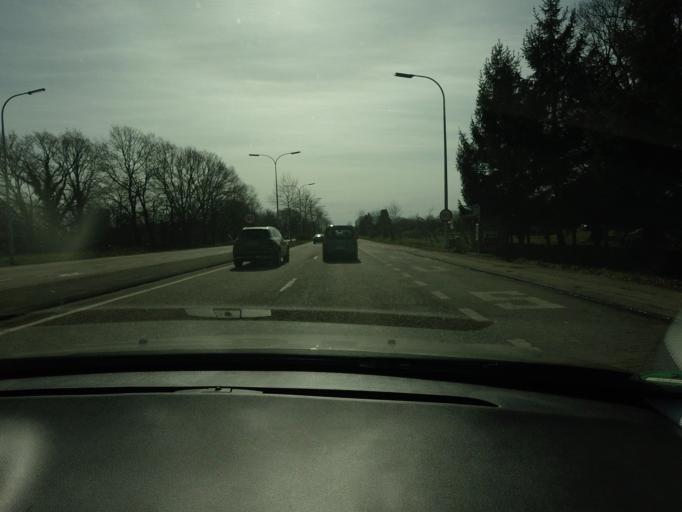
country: BE
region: Flanders
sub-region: Provincie Limburg
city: Zonhoven
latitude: 50.9850
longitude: 5.3592
